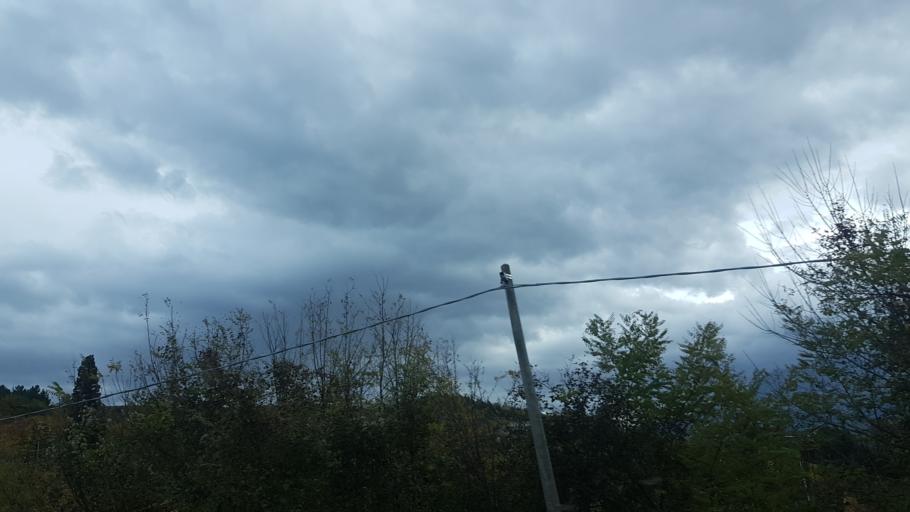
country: IT
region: Abruzzo
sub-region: Provincia dell' Aquila
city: Progetto Case Bazzano
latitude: 42.3568
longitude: 13.4297
